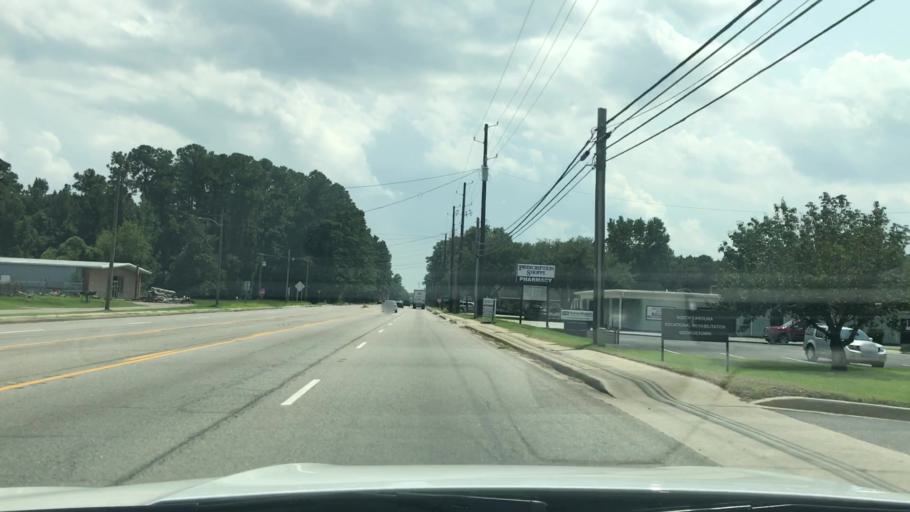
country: US
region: South Carolina
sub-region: Georgetown County
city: Georgetown
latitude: 33.3997
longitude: -79.2894
